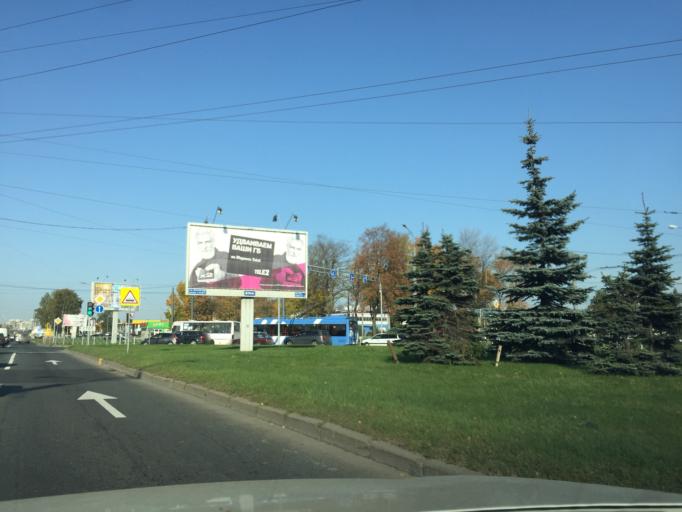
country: RU
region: Leningrad
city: Akademicheskoe
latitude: 60.0035
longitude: 30.4362
